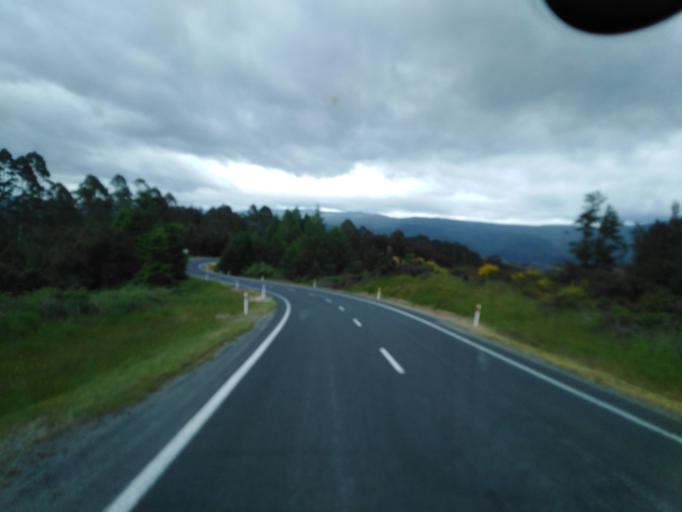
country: NZ
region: Tasman
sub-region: Tasman District
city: Wakefield
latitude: -41.6292
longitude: 172.7083
